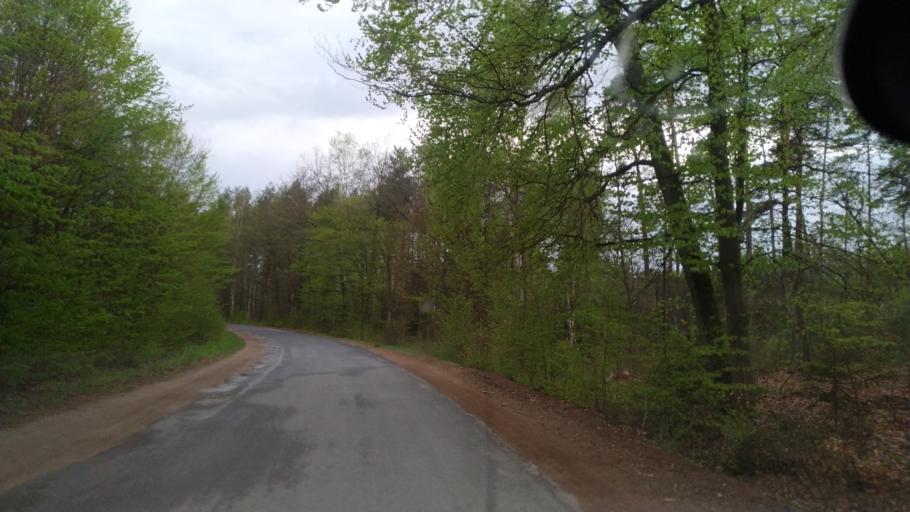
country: PL
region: Pomeranian Voivodeship
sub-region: Powiat starogardzki
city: Osiek
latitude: 53.7029
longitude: 18.5705
